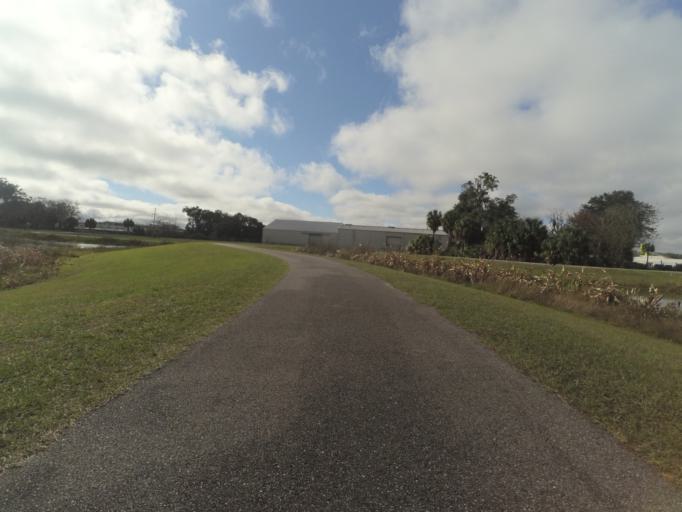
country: US
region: Florida
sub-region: Alachua County
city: Gainesville
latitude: 29.6417
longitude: -82.3234
